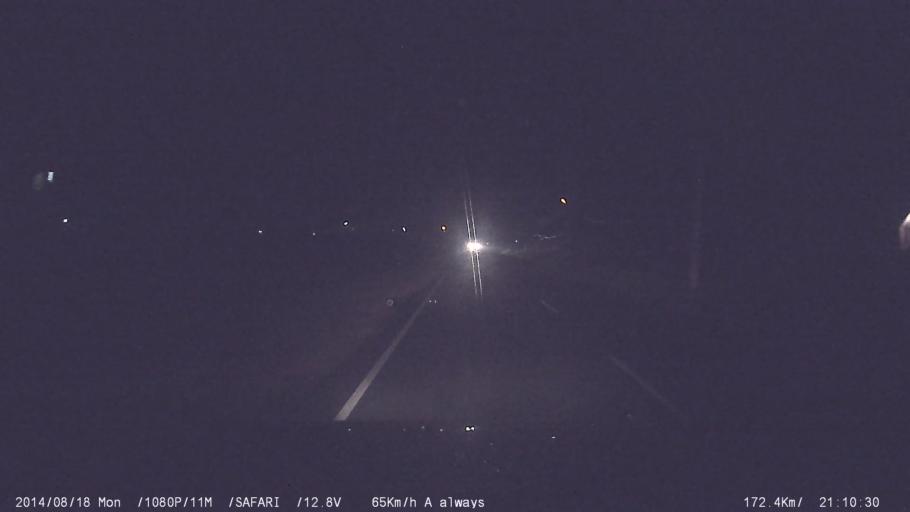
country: IN
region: Kerala
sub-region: Thrissur District
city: Trichur
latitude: 10.5399
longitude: 76.2839
